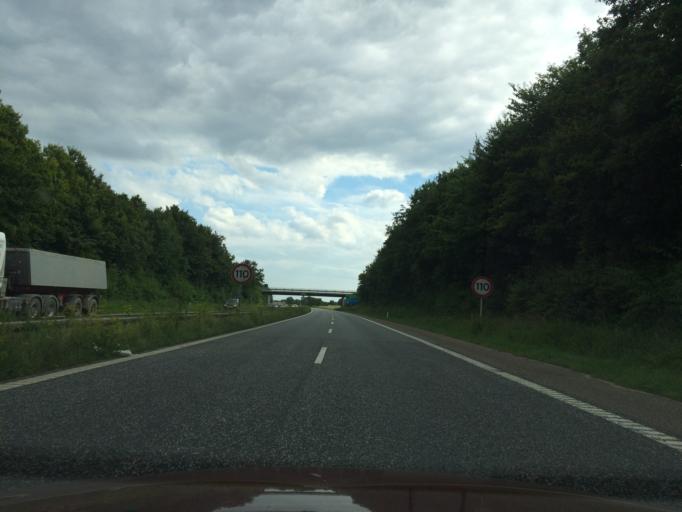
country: DK
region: Central Jutland
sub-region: Arhus Kommune
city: Logten
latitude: 56.2850
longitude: 10.3308
